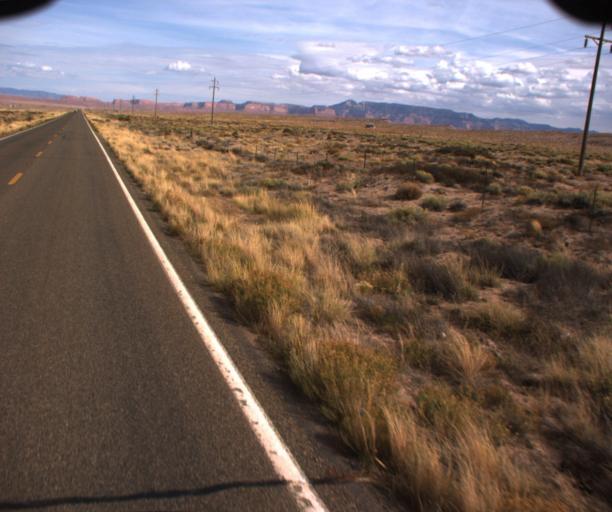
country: US
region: Arizona
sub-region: Apache County
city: Many Farms
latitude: 36.4803
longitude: -109.5100
